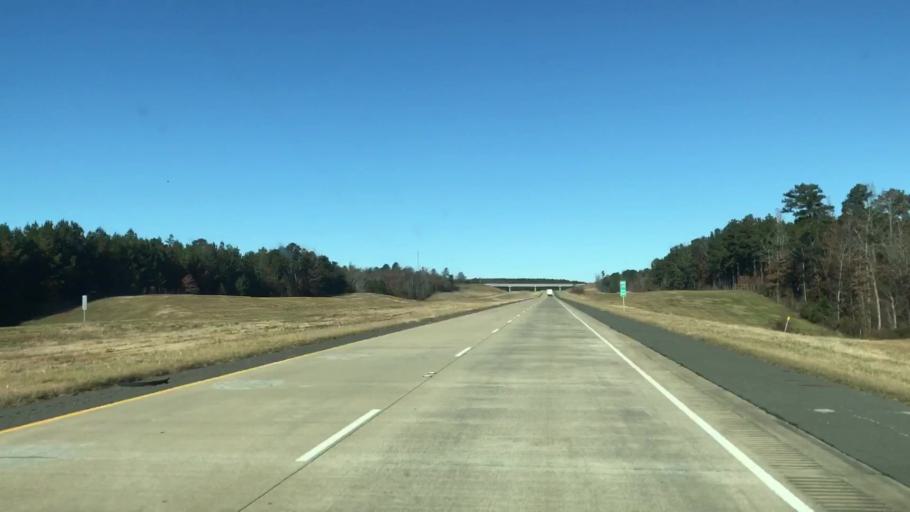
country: US
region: Louisiana
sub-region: Caddo Parish
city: Vivian
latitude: 32.9163
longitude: -93.8781
